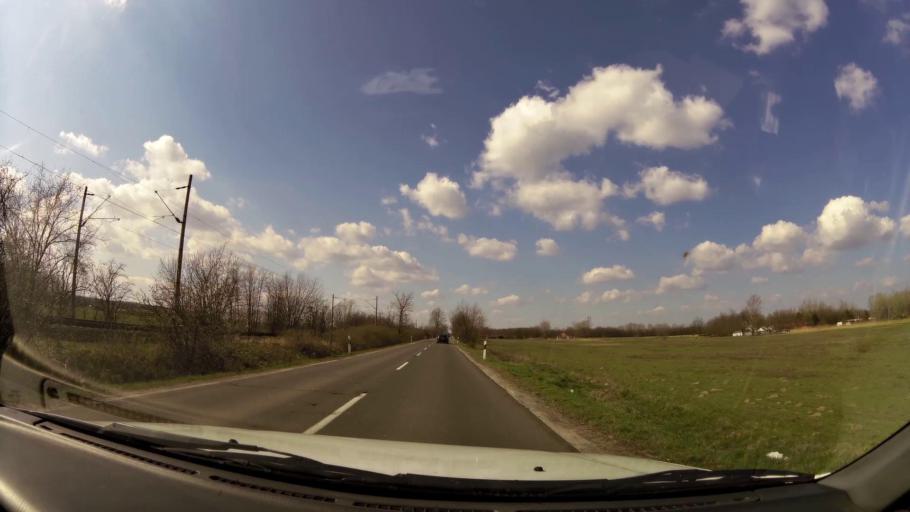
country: HU
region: Pest
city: Nagykata
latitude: 47.3898
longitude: 19.7718
